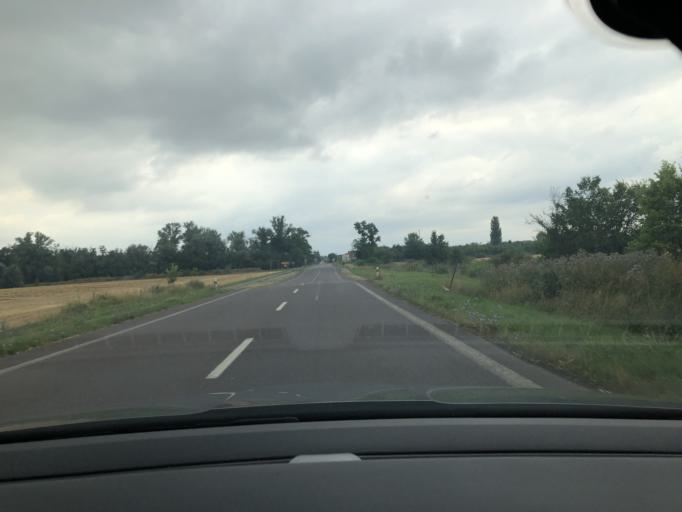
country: CZ
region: South Moravian
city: Hevlin
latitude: 48.7458
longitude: 16.3811
